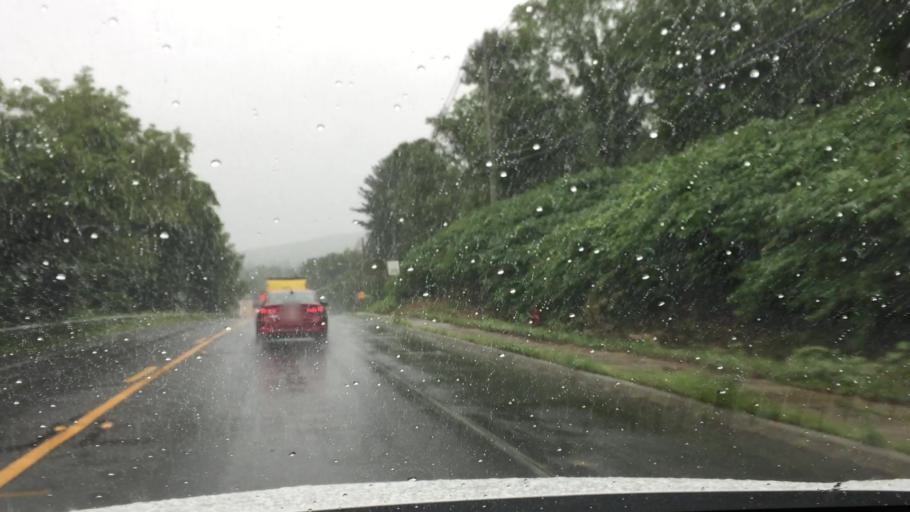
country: US
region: Massachusetts
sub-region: Berkshire County
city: Lanesborough
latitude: 42.5096
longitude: -73.2318
